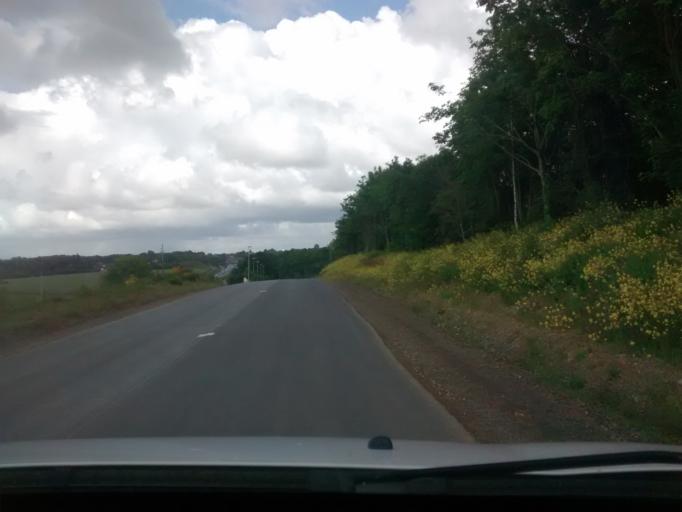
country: FR
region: Brittany
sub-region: Departement d'Ille-et-Vilaine
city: Cesson-Sevigne
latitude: 48.1092
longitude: -1.5943
